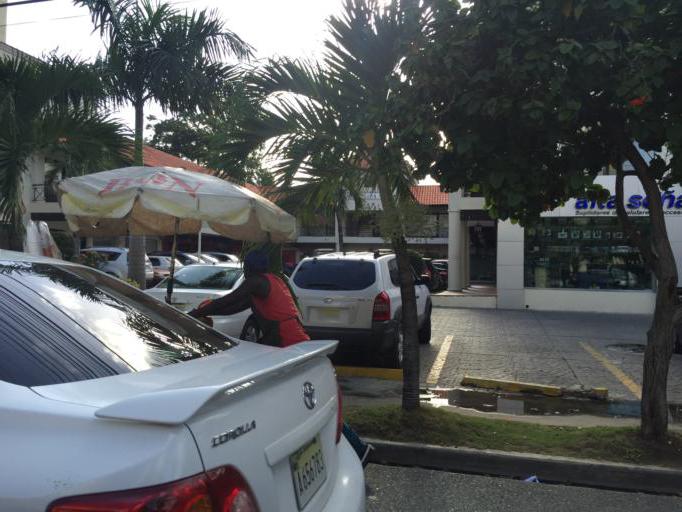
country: DO
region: Nacional
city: La Julia
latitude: 18.4752
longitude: -69.9358
